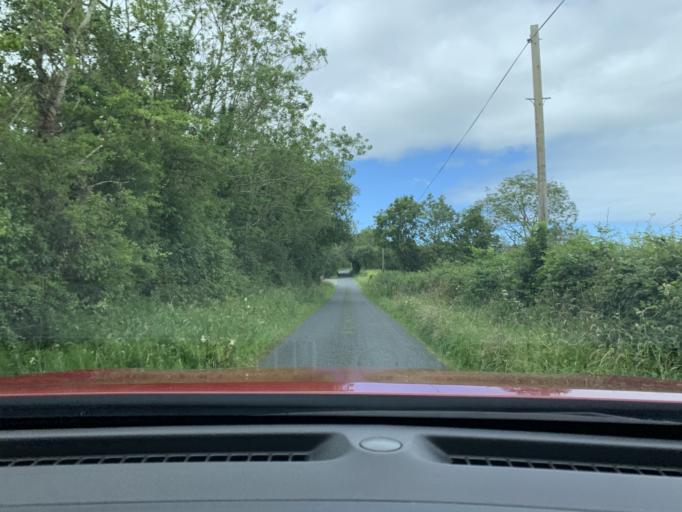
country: IE
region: Connaught
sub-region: Sligo
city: Sligo
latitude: 54.3300
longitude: -8.4738
